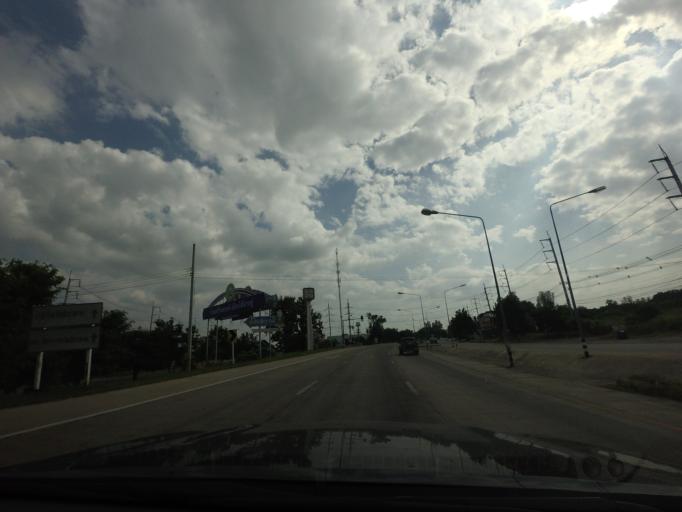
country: TH
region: Lop Buri
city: Chai Badan
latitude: 15.2179
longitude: 101.1274
